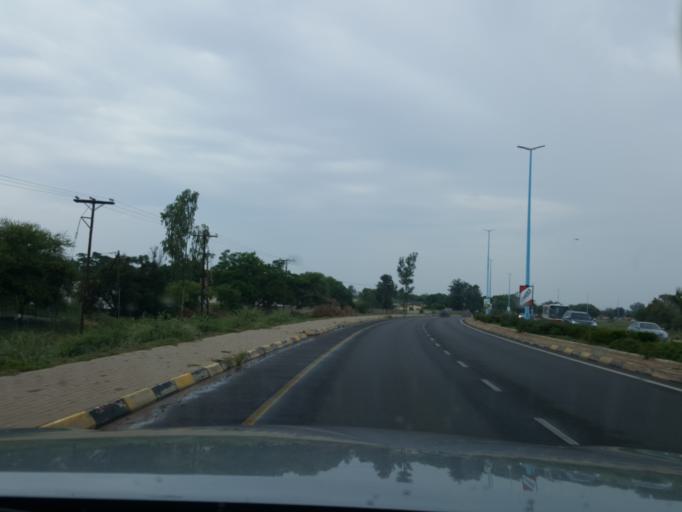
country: BW
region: South East
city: Gaborone
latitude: -24.6164
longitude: 25.9305
